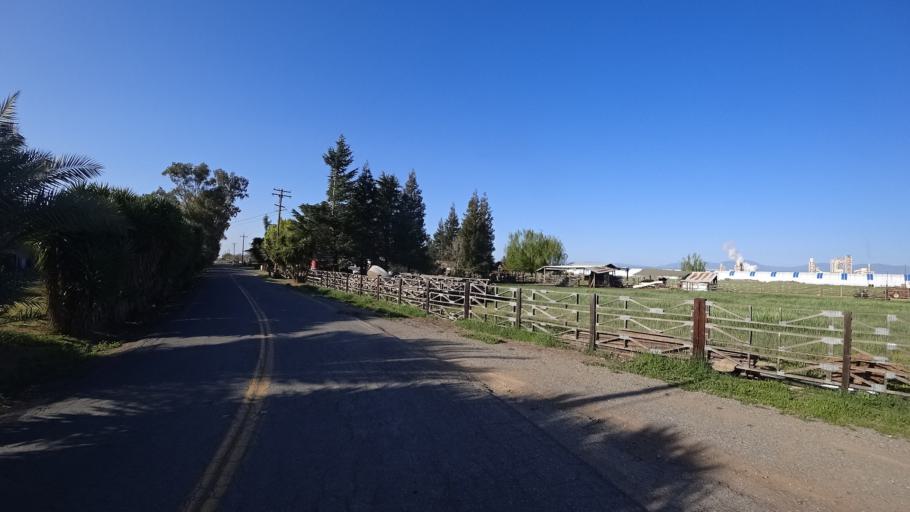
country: US
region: California
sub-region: Glenn County
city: Willows
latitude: 39.5166
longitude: -122.2299
